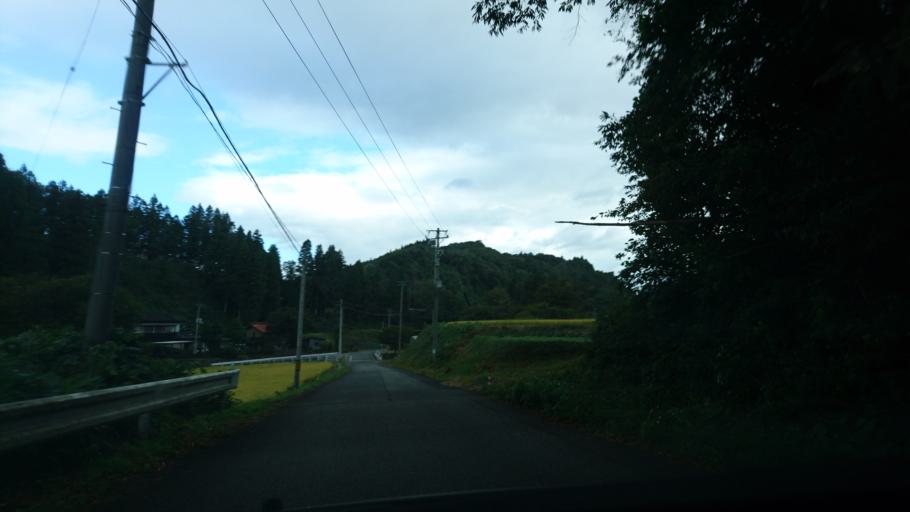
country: JP
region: Iwate
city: Ichinoseki
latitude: 38.9112
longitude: 141.0782
